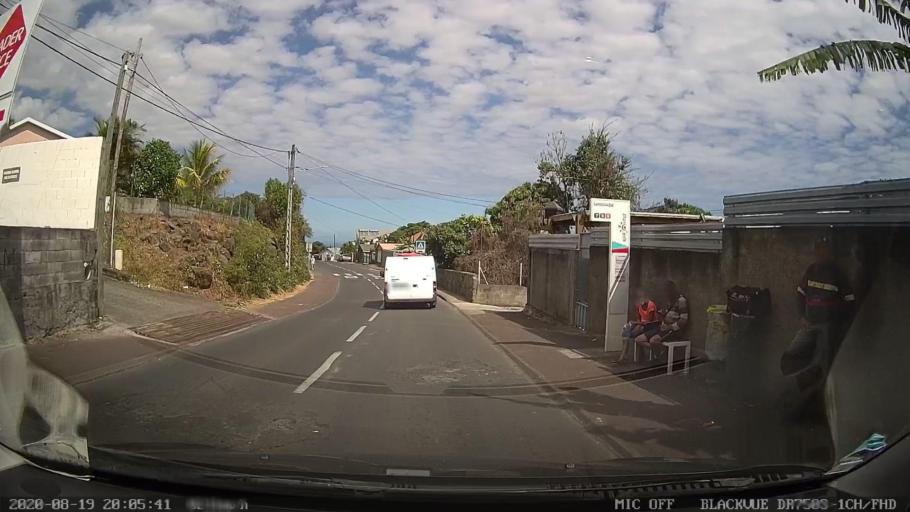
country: RE
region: Reunion
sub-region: Reunion
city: La Possession
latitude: -20.9547
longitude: 55.3387
